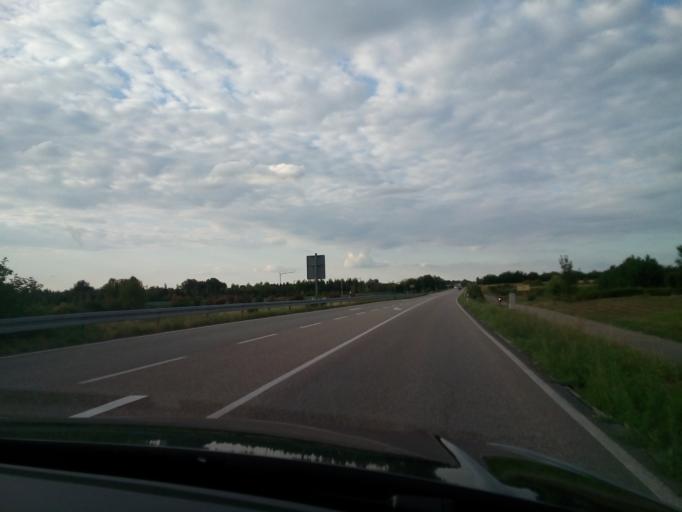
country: DE
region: Baden-Wuerttemberg
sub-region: Freiburg Region
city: Appenweier
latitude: 48.5459
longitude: 7.9780
